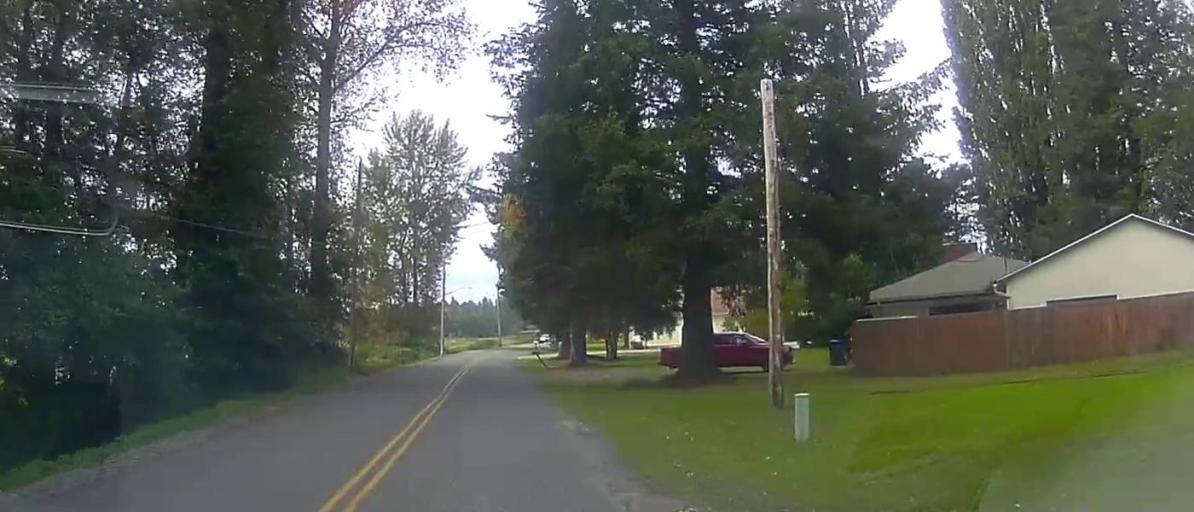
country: US
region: Washington
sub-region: Skagit County
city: Sedro-Woolley
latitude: 48.4983
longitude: -122.2508
